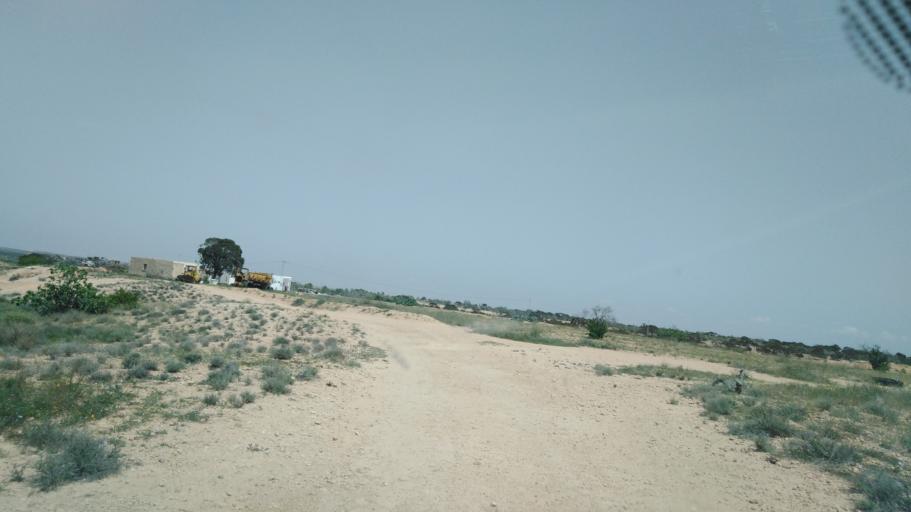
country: TN
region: Safaqis
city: Sfax
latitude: 34.7201
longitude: 10.5662
